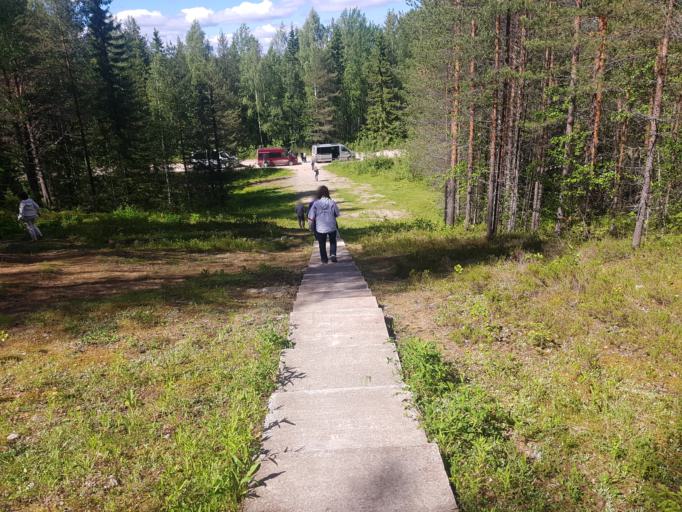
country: RU
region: Republic of Karelia
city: Kalevala
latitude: 65.2605
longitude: 30.9325
